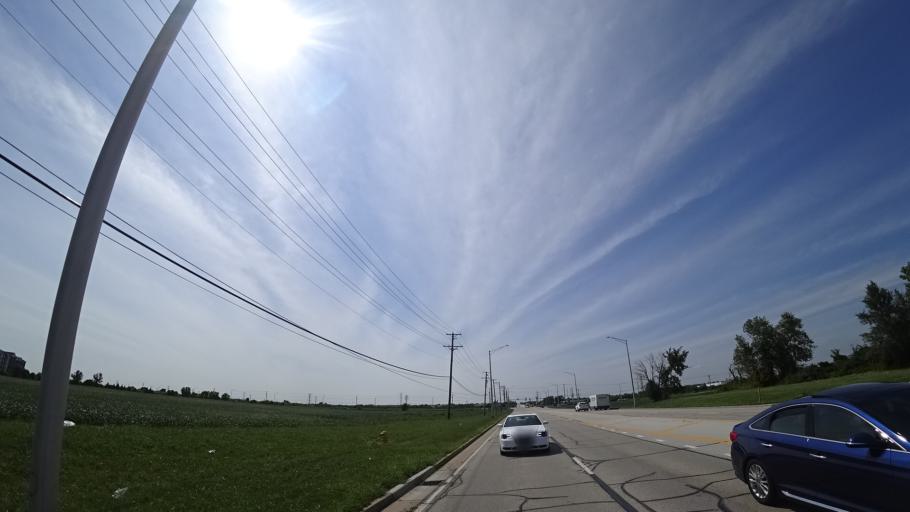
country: US
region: Illinois
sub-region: Will County
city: Frankfort Square
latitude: 41.5437
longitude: -87.8087
